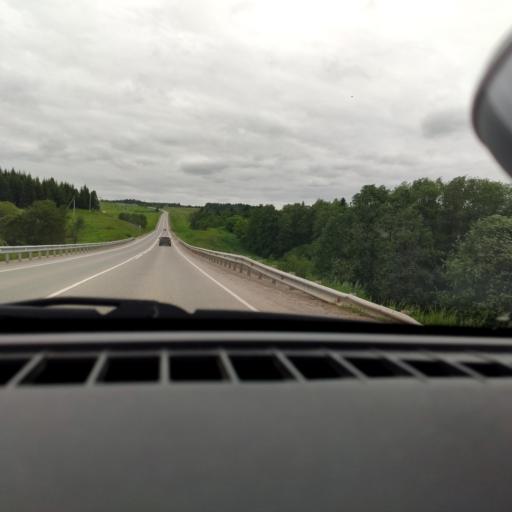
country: RU
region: Perm
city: Kultayevo
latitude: 57.9002
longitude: 55.7856
